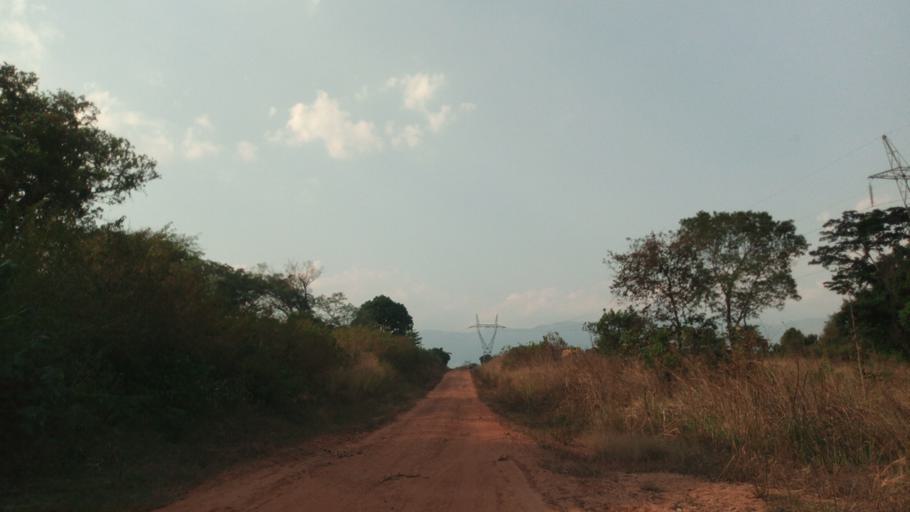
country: TZ
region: Kigoma
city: Kigoma
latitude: -5.1912
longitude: 28.8917
